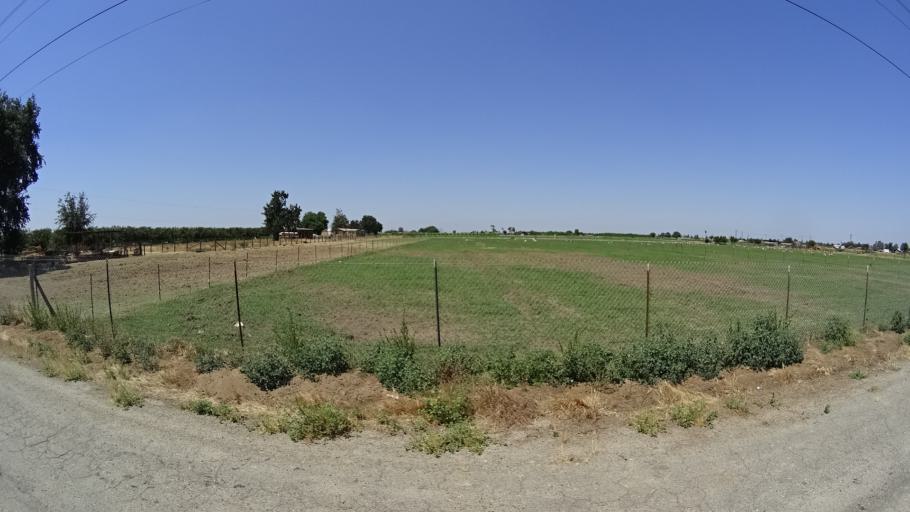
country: US
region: California
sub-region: Fresno County
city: Kingsburg
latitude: 36.4950
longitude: -119.5389
